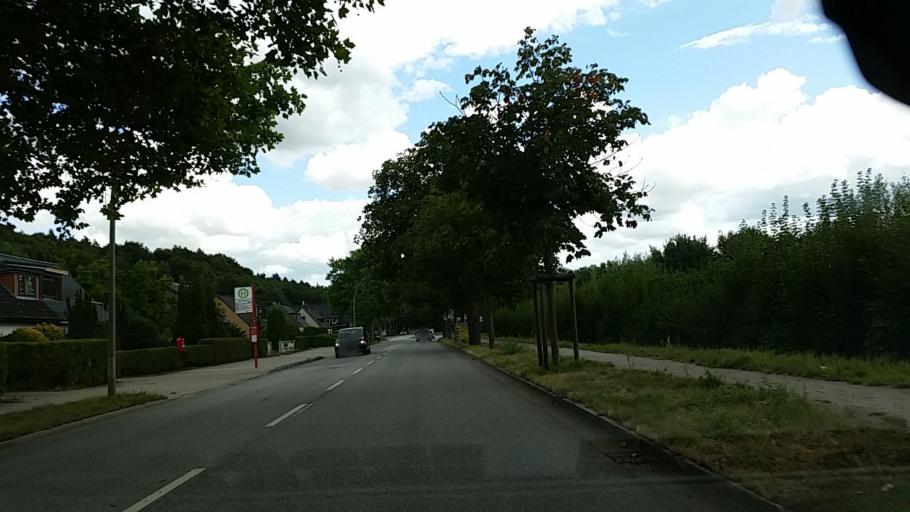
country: DE
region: Schleswig-Holstein
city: Bornsen
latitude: 53.4726
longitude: 10.2600
